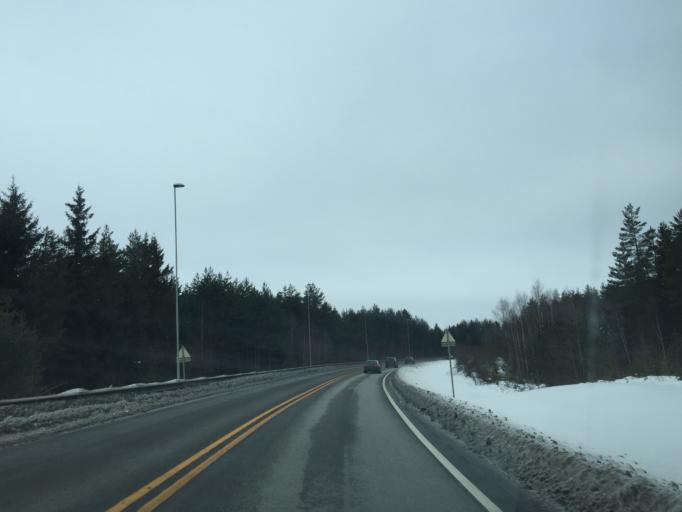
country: NO
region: Hedmark
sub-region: Loten
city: Loten
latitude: 60.7754
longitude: 11.3061
